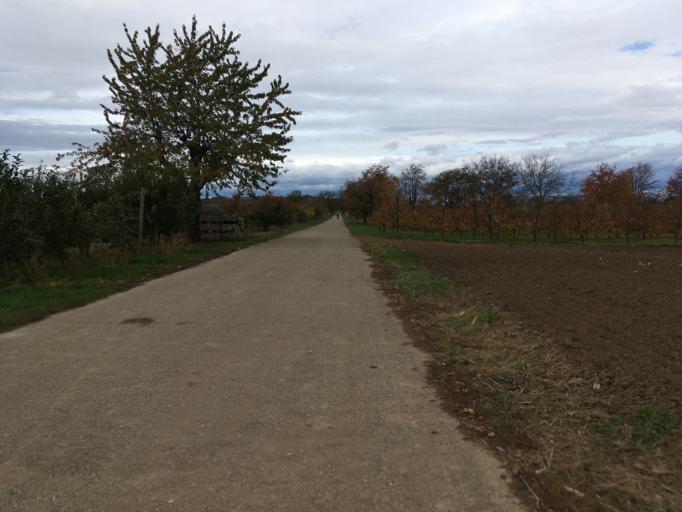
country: DE
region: Baden-Wuerttemberg
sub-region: Freiburg Region
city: Wyhl
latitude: 48.1385
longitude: 7.6494
